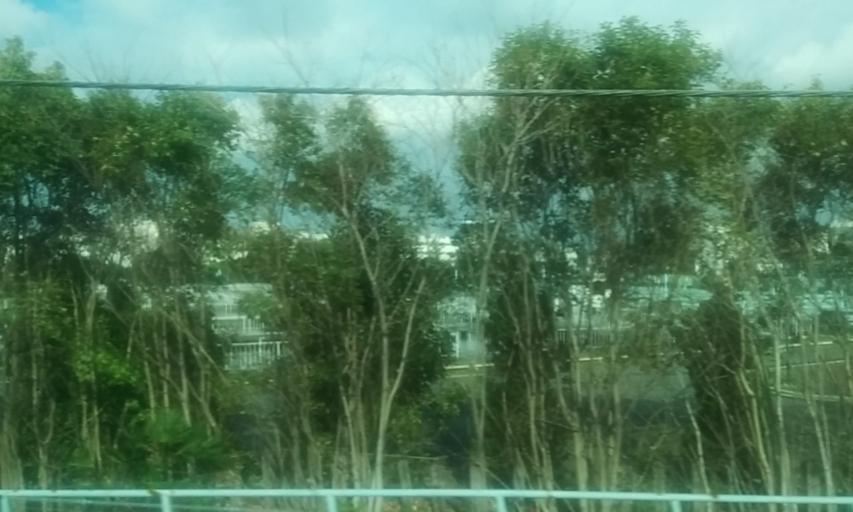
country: JP
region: Kanagawa
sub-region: Kawasaki-shi
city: Kawasaki
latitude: 35.5166
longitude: 139.6793
